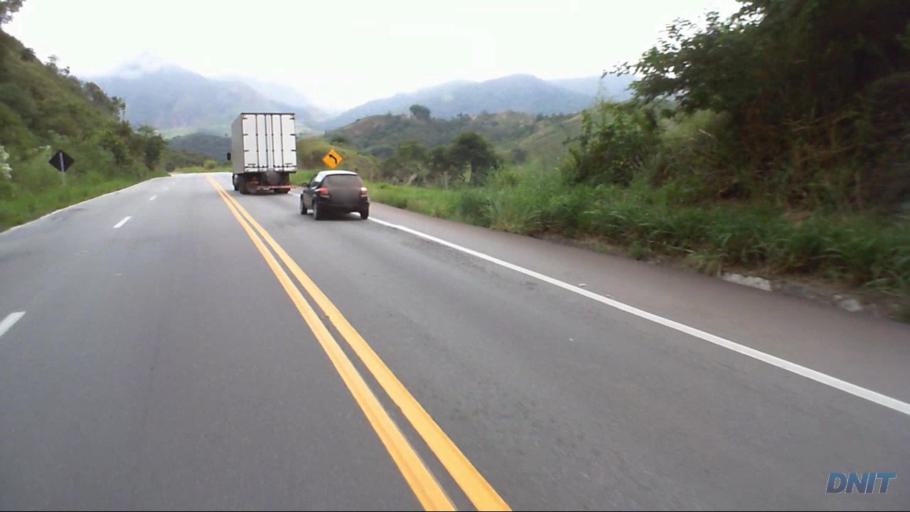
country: BR
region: Minas Gerais
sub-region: Nova Era
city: Nova Era
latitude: -19.6678
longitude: -42.9660
